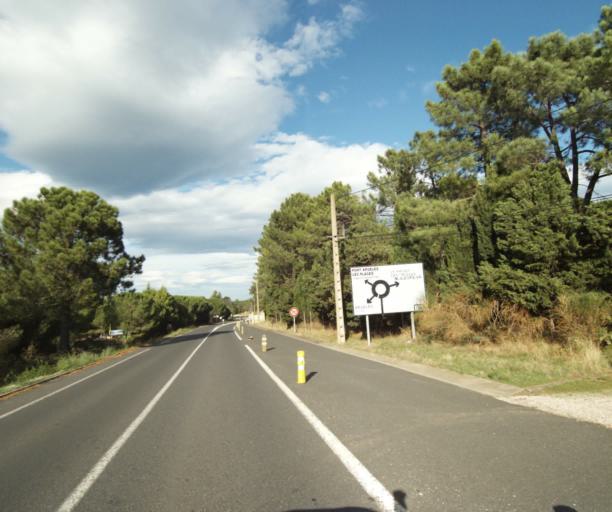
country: FR
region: Languedoc-Roussillon
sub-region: Departement des Pyrenees-Orientales
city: Argelers
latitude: 42.5383
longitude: 3.0348
